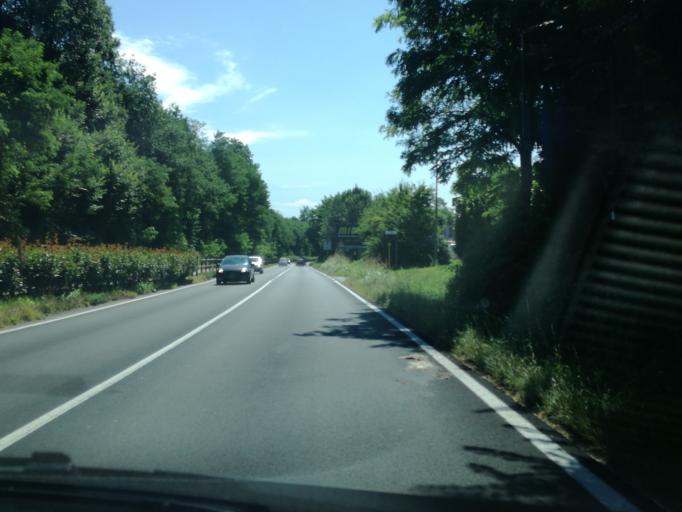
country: IT
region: Lombardy
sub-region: Provincia di Bergamo
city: Terno d'Isola
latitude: 45.6902
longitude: 9.5220
